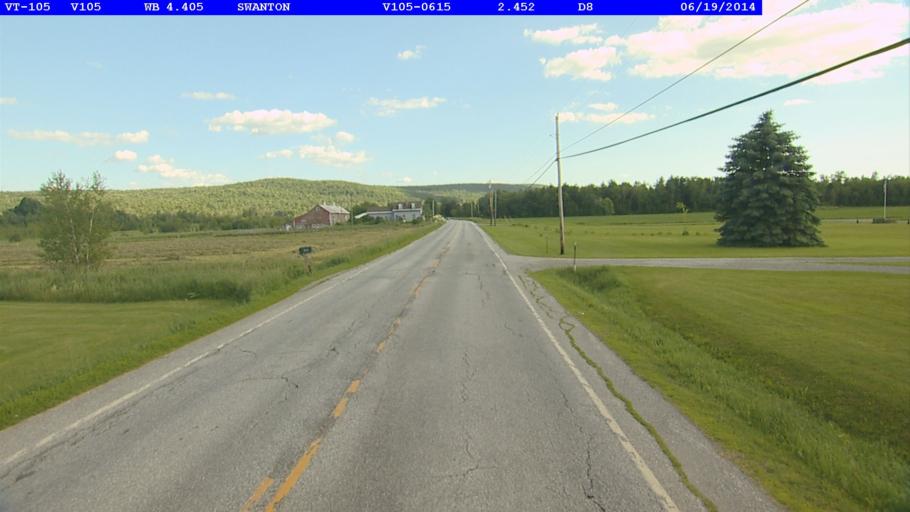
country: US
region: Vermont
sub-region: Franklin County
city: Saint Albans
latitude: 44.8677
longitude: -73.0328
